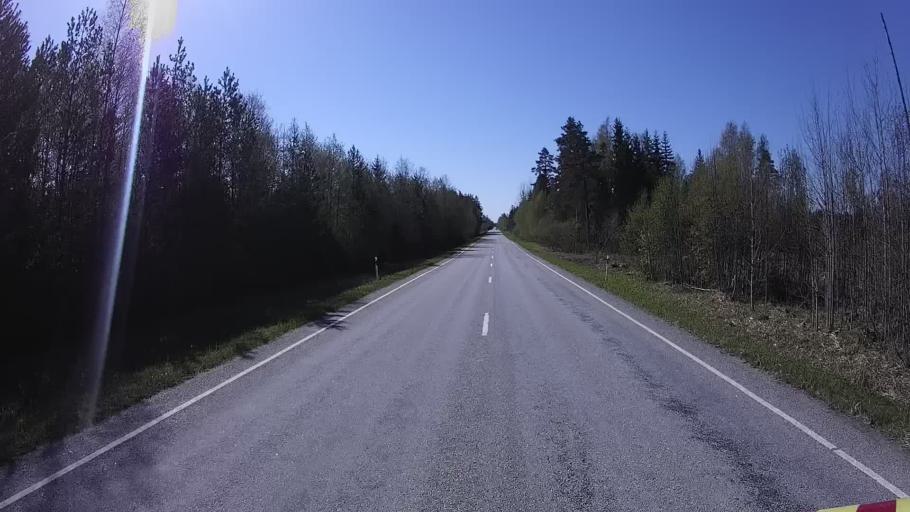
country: EE
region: Raplamaa
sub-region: Jaervakandi vald
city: Jarvakandi
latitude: 58.8130
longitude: 24.8058
